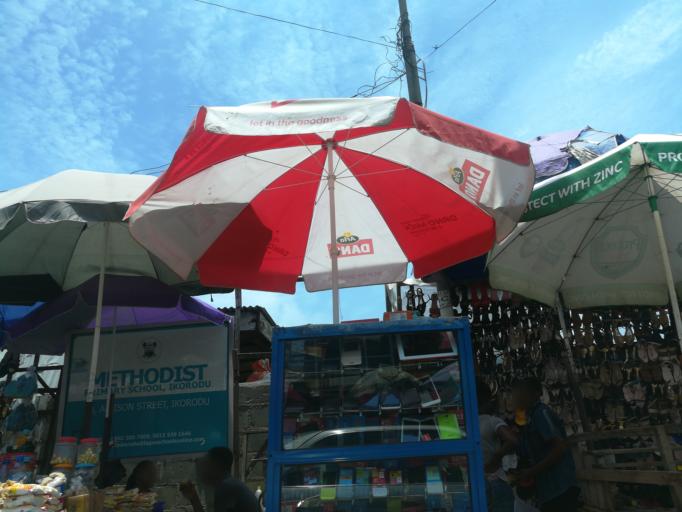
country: NG
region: Lagos
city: Ikorodu
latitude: 6.6191
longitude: 3.5023
